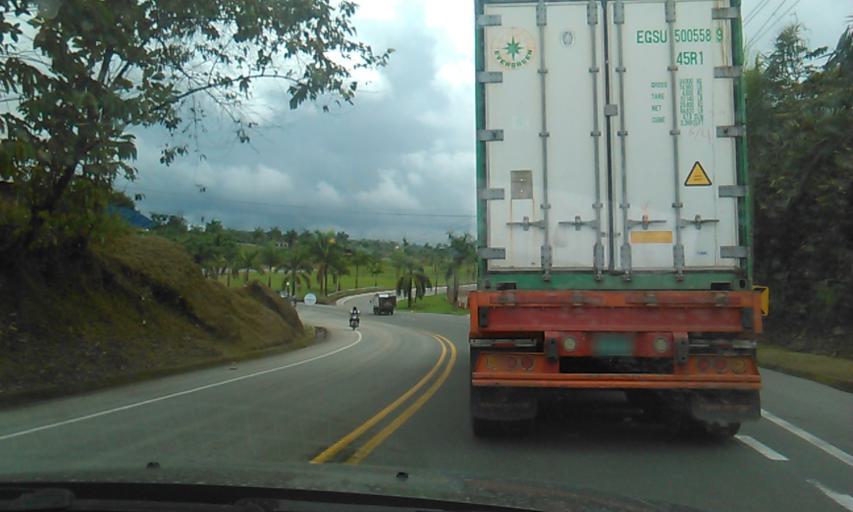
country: CO
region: Valle del Cauca
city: Buenaventura
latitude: 3.8809
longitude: -76.9659
